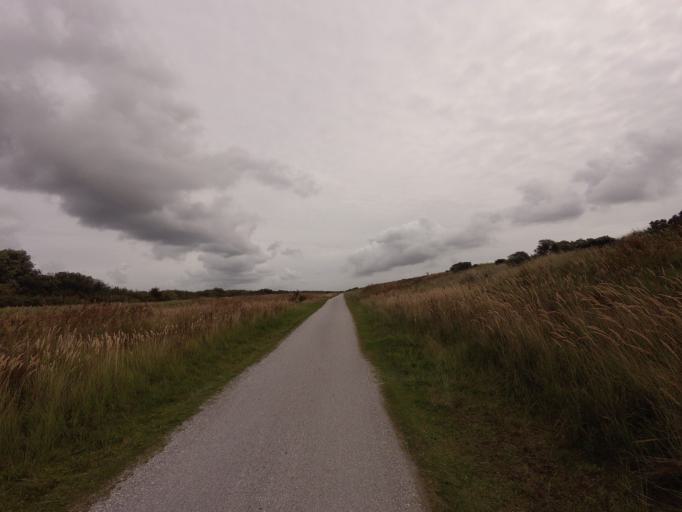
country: NL
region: Friesland
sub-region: Gemeente Ameland
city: Hollum
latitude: 53.4583
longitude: 5.6730
